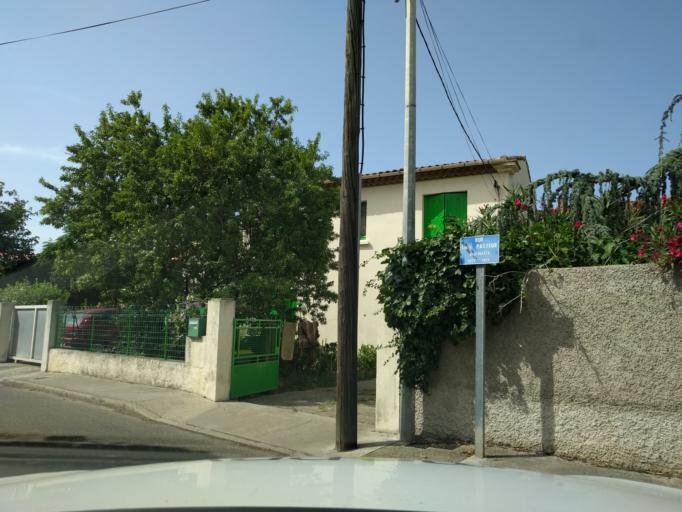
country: FR
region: Languedoc-Roussillon
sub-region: Departement de l'Aude
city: Carcassonne
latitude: 43.2134
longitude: 2.3367
